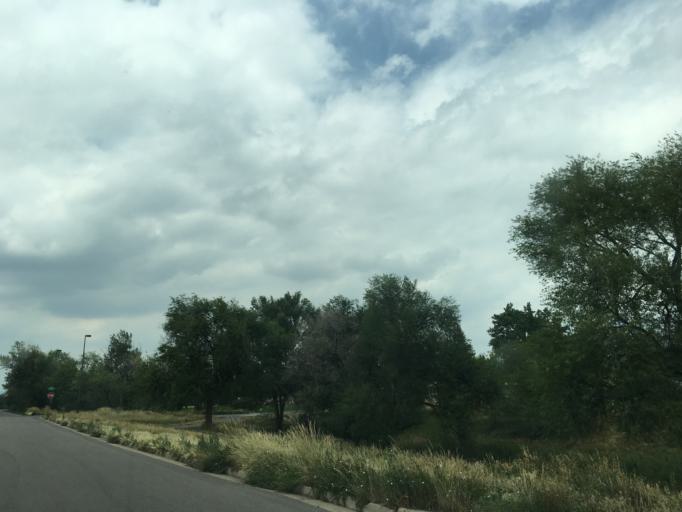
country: US
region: Colorado
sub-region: Arapahoe County
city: Sheridan
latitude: 39.6846
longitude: -105.0332
